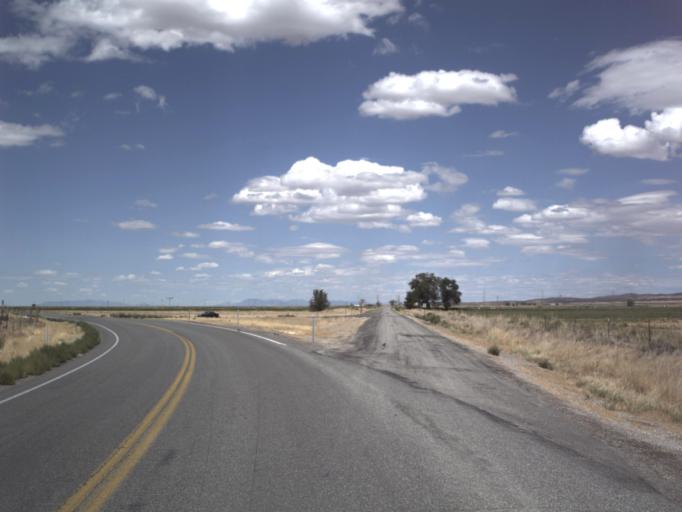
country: US
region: Utah
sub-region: Millard County
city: Delta
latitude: 39.2014
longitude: -112.4099
